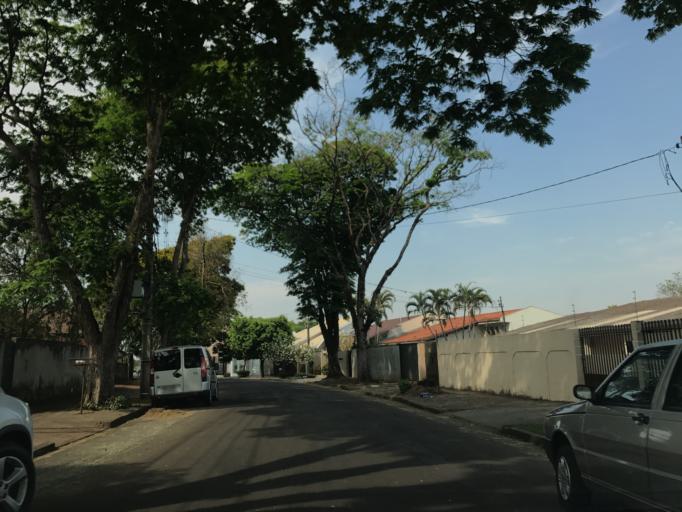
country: BR
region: Parana
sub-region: Maringa
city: Maringa
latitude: -23.4369
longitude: -51.9492
